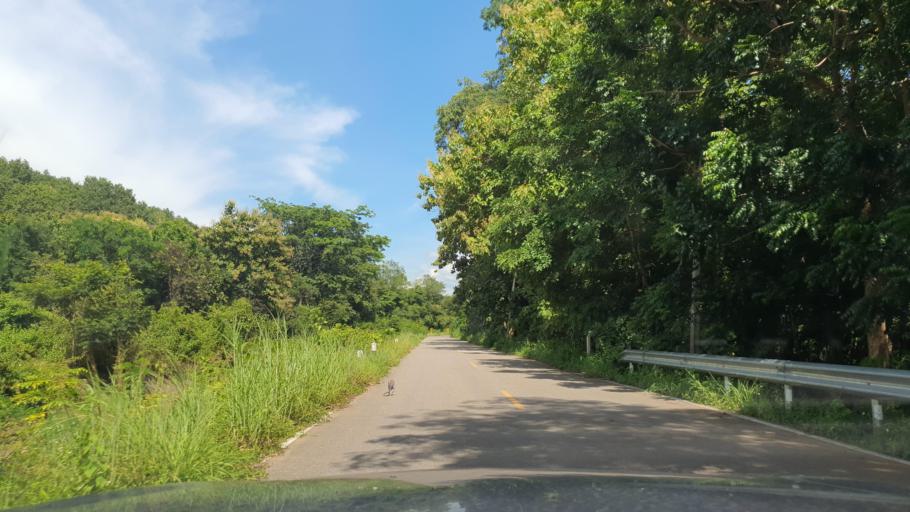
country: TH
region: Chiang Mai
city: Mae On
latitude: 18.7450
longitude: 99.1897
